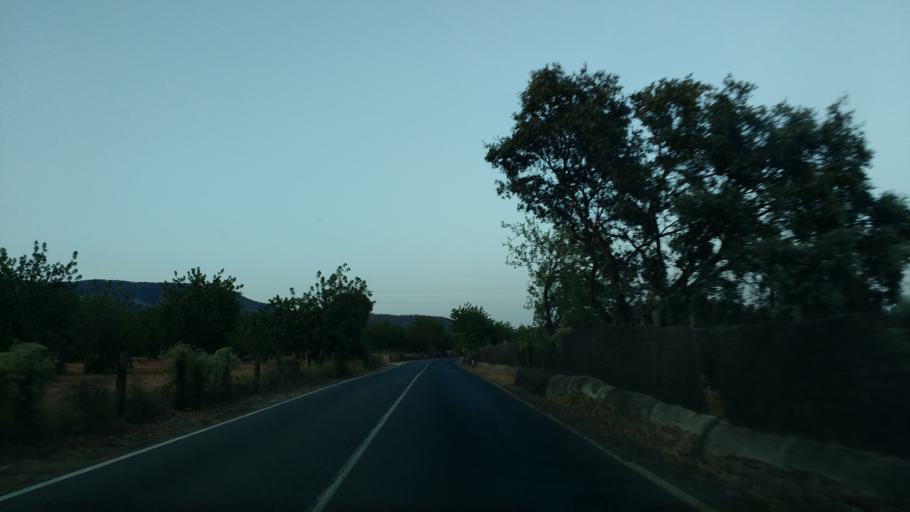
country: ES
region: Balearic Islands
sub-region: Illes Balears
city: Bunyola
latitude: 39.6659
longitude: 2.6929
